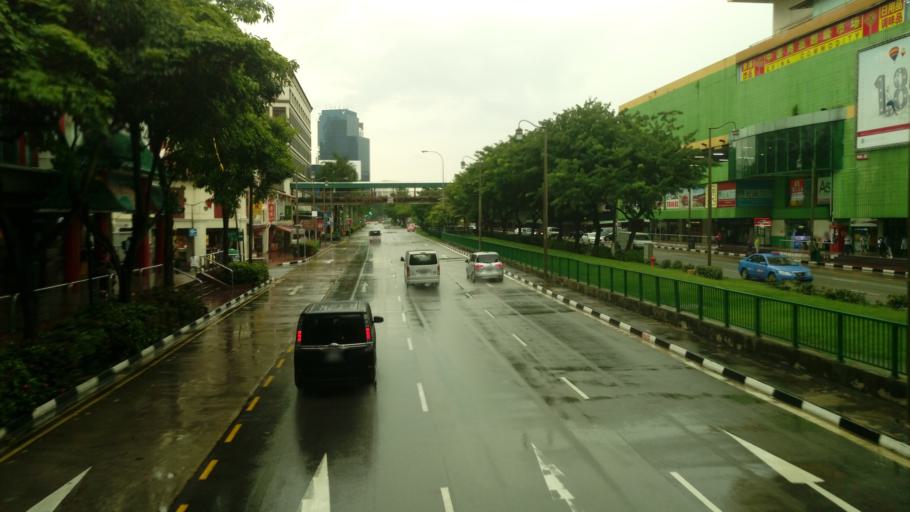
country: SG
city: Singapore
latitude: 1.2849
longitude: 103.8431
